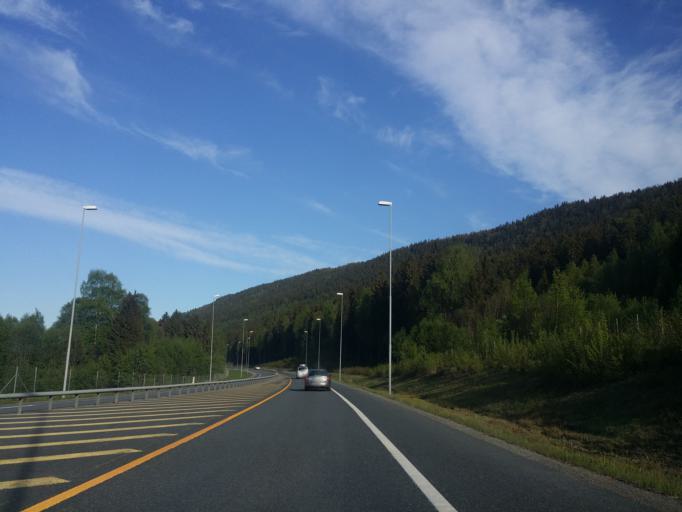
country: NO
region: Buskerud
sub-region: Nedre Eiker
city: Mjondalen
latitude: 59.7441
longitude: 10.0711
